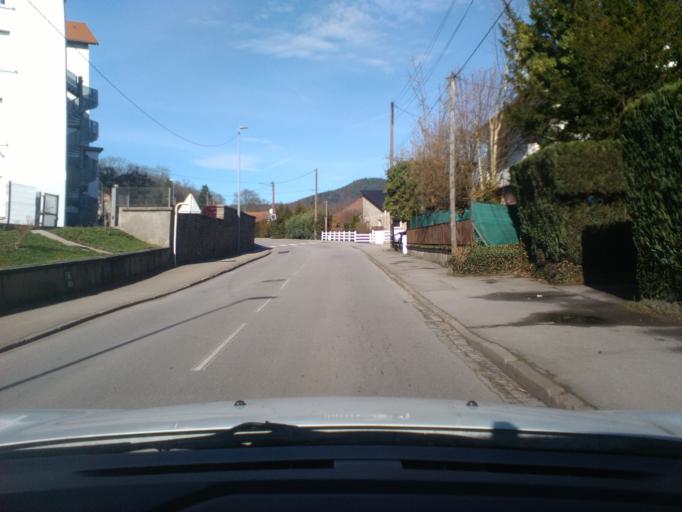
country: FR
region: Lorraine
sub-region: Departement des Vosges
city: Saint-Die-des-Vosges
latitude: 48.2945
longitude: 6.9513
